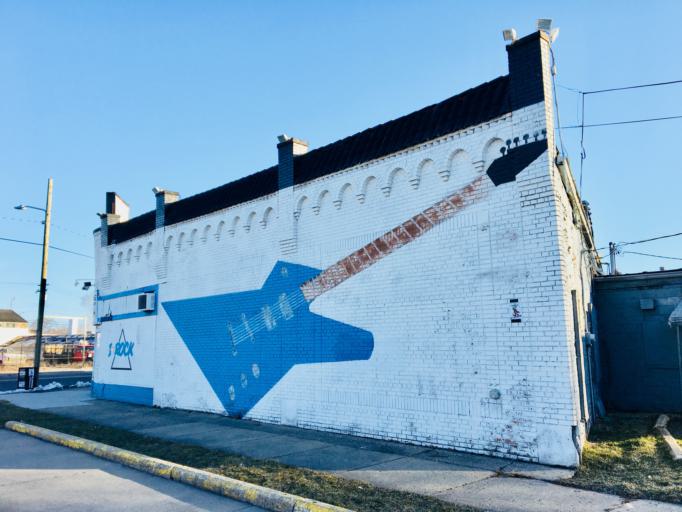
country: US
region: Michigan
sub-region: Wayne County
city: Harper Woods
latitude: 42.4108
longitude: -82.9441
